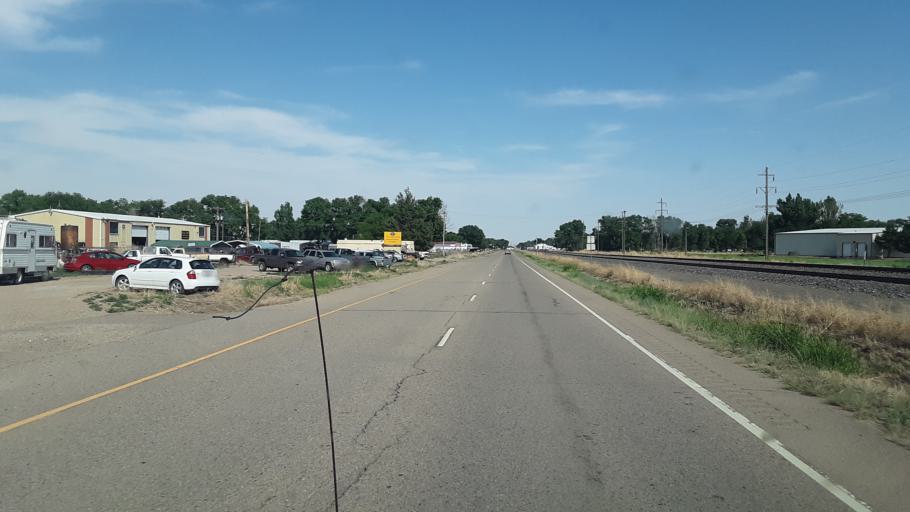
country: US
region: Colorado
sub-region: Otero County
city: Rocky Ford
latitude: 38.0606
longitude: -103.7387
